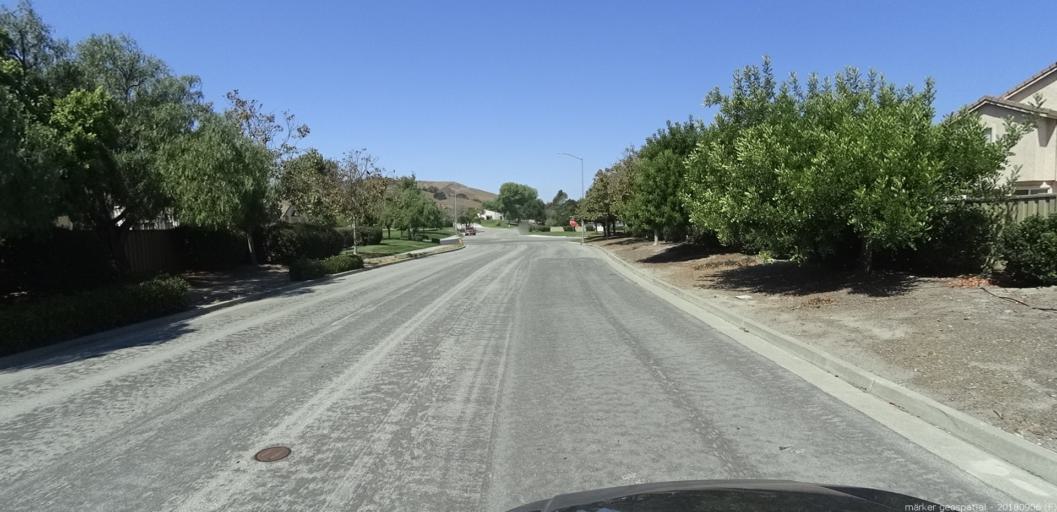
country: US
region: California
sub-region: Monterey County
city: Salinas
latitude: 36.6048
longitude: -121.6447
